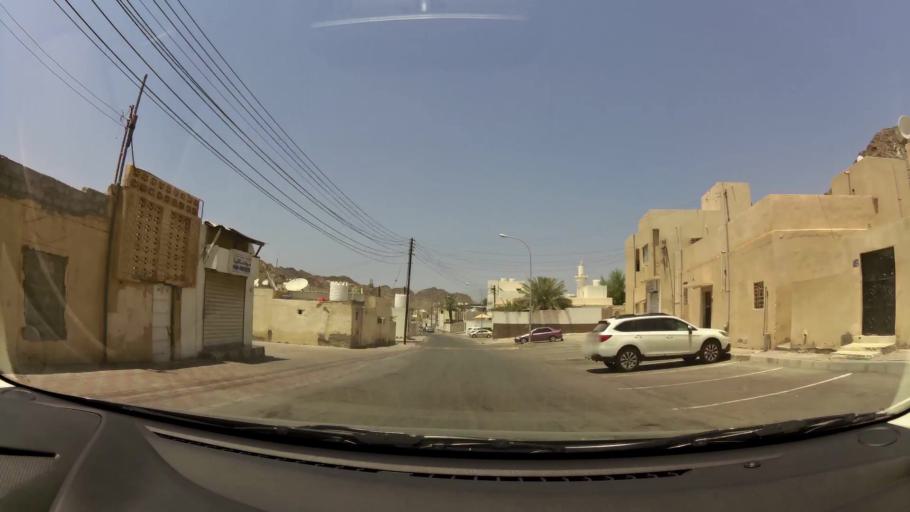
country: OM
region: Muhafazat Masqat
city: Muscat
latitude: 23.6187
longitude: 58.5538
